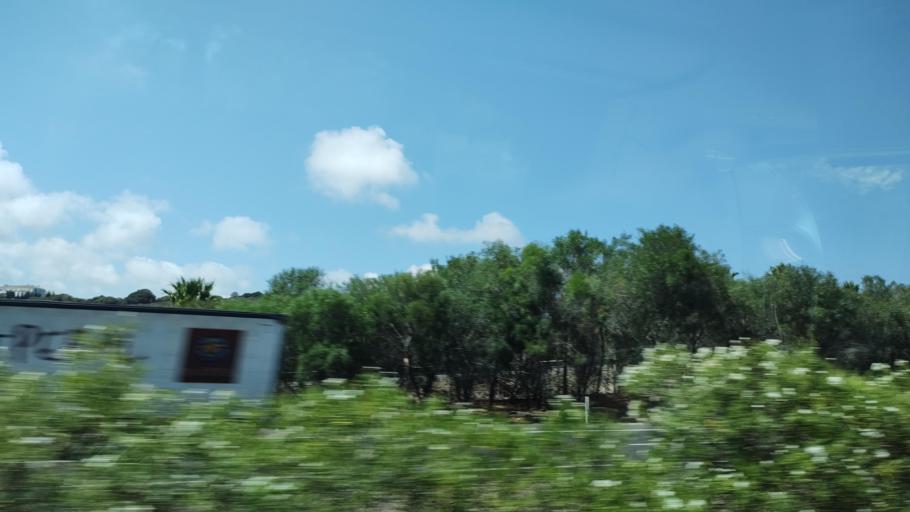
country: ES
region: Andalusia
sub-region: Provincia de Cadiz
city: San Roque
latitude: 36.2606
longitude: -5.3298
